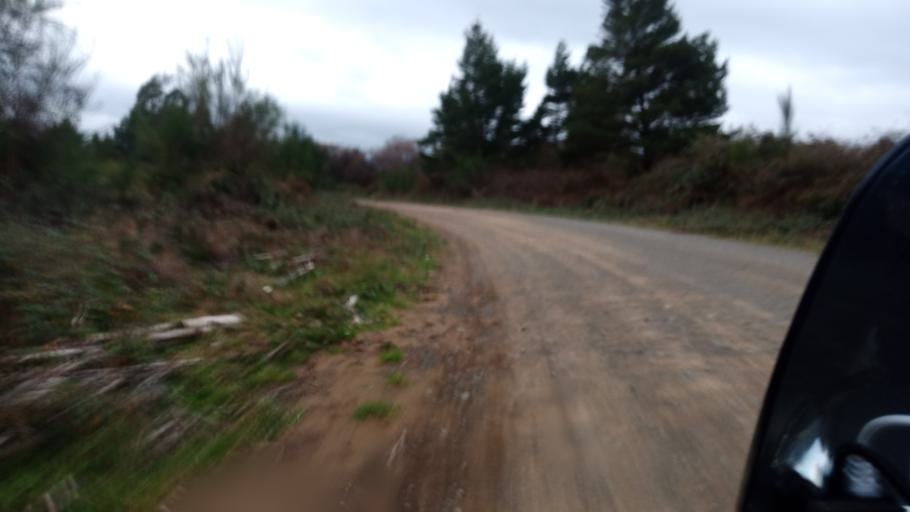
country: NZ
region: Bay of Plenty
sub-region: Whakatane District
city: Murupara
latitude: -38.6384
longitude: 176.7206
